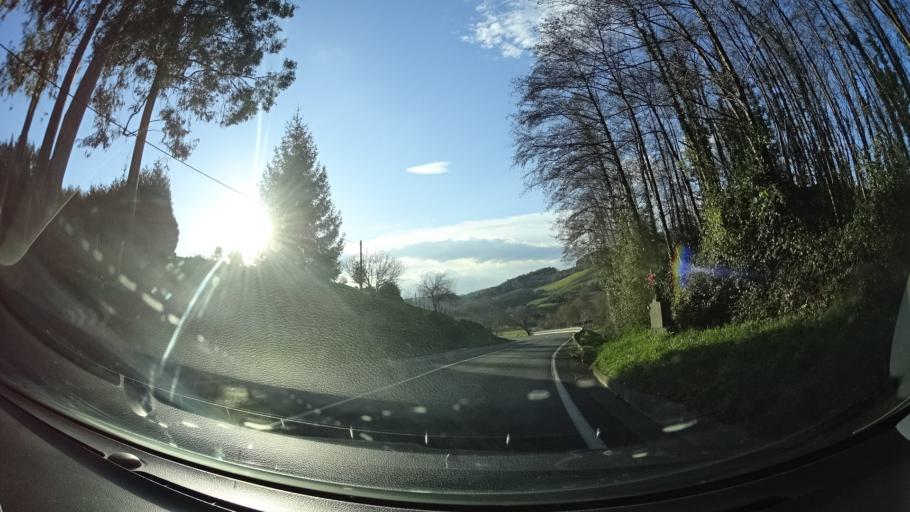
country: ES
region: Basque Country
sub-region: Bizkaia
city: Mungia
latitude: 43.3774
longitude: -2.7942
